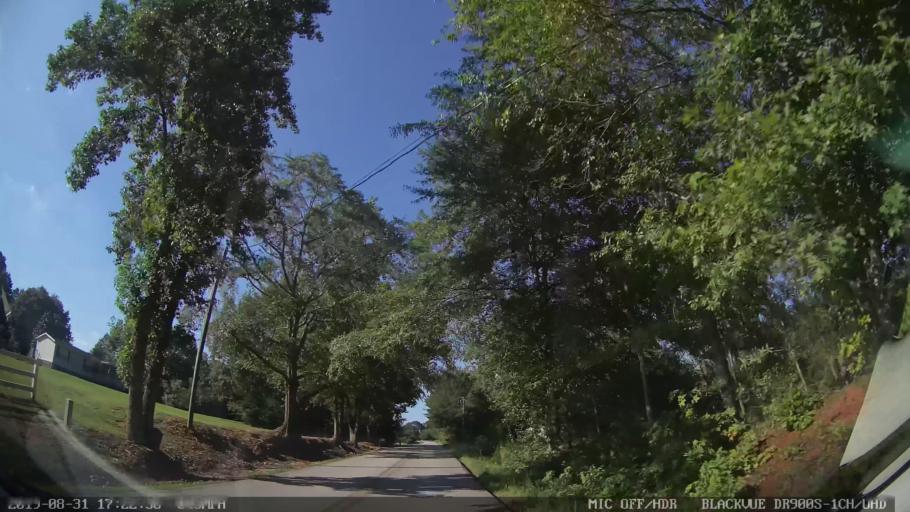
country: US
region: South Carolina
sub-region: Spartanburg County
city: Boiling Springs
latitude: 35.0770
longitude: -81.9381
